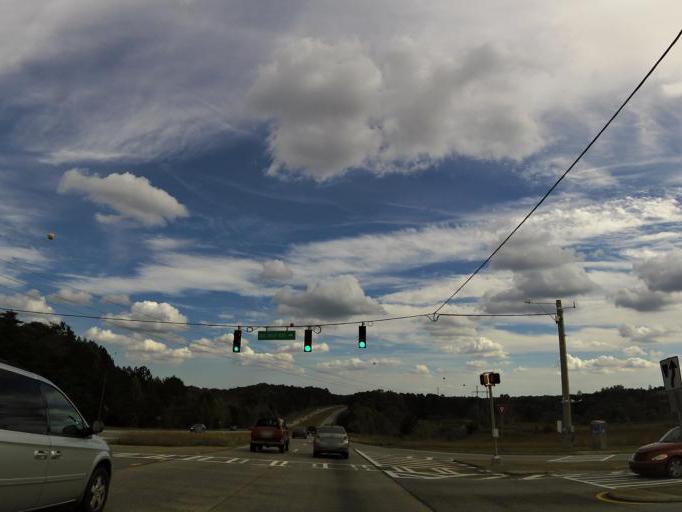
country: US
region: Georgia
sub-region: Pickens County
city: Jasper
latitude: 34.4464
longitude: -84.4456
